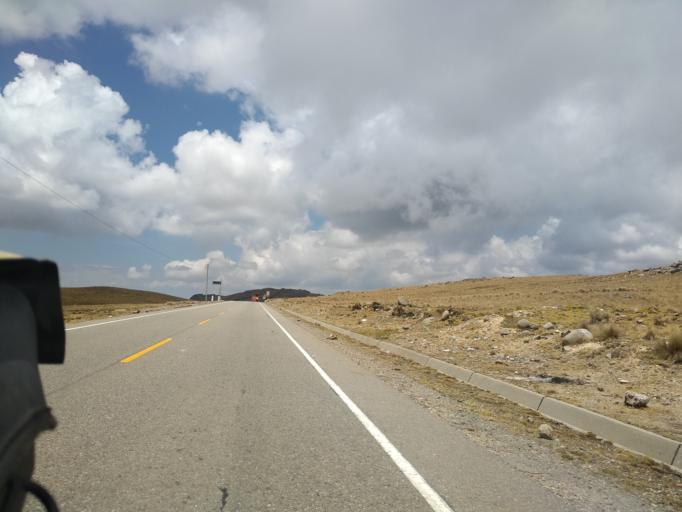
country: PE
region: La Libertad
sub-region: Provincia de Santiago de Chuco
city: Quiruvilca
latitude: -7.9665
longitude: -78.1991
